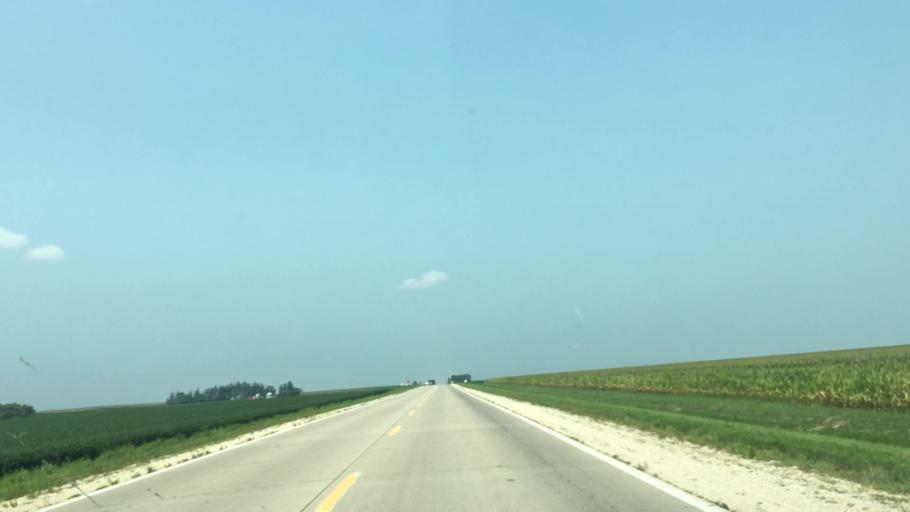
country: US
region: Iowa
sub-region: Fayette County
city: Oelwein
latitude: 42.6897
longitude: -91.8051
